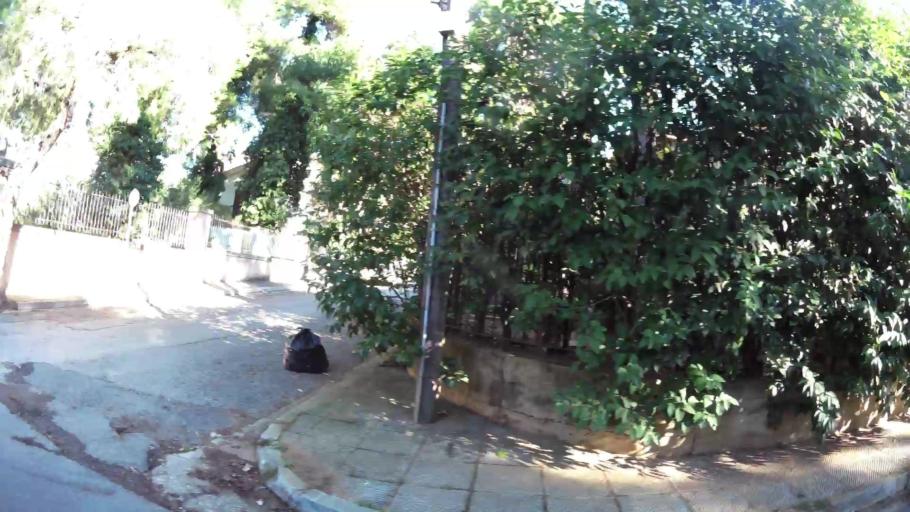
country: GR
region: Attica
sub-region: Nomarchia Anatolikis Attikis
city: Drosia
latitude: 38.1065
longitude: 23.8622
